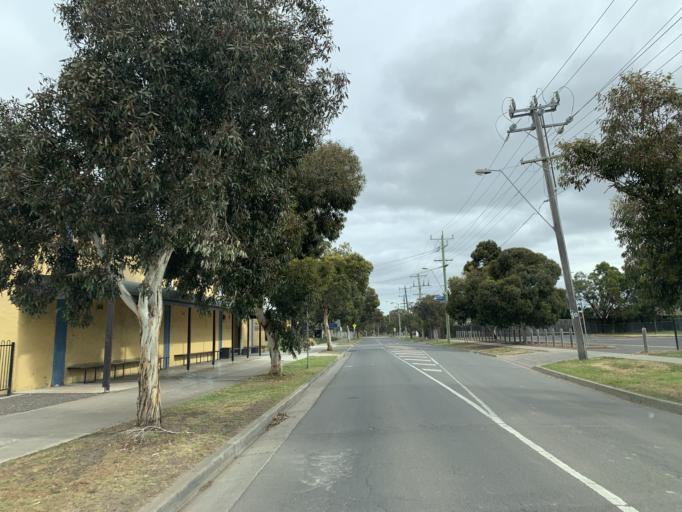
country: AU
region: Victoria
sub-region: Brimbank
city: St Albans
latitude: -37.7468
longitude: 144.7997
